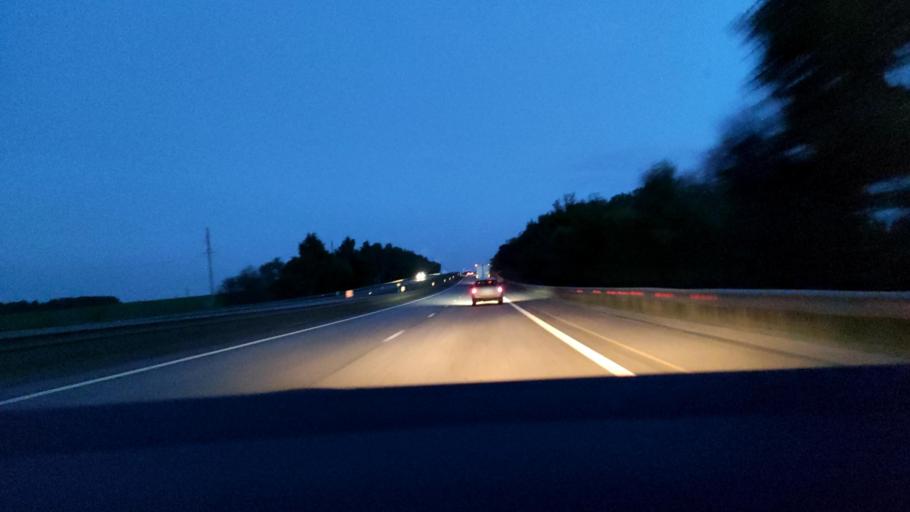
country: RU
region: Voronezj
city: Ramon'
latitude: 51.9192
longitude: 39.2198
